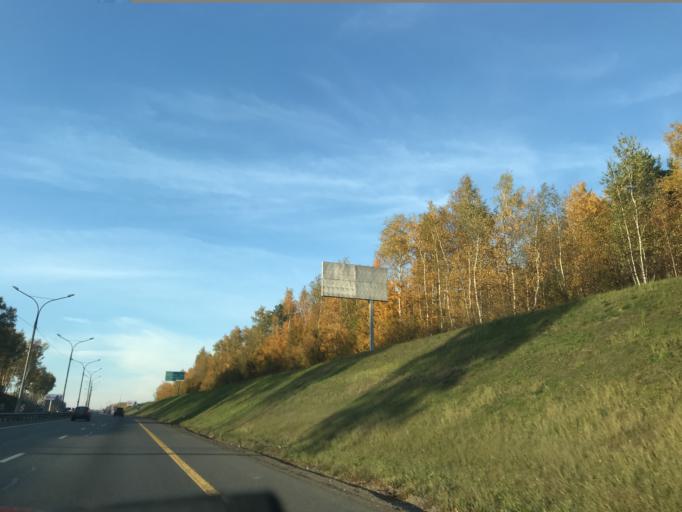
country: RU
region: Moskovskaya
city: Gorki-Leninskiye
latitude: 55.5038
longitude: 37.8377
